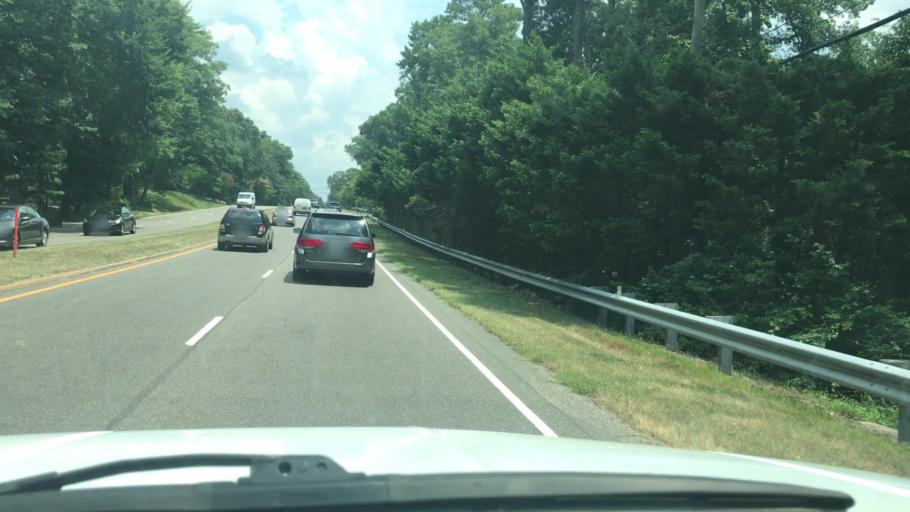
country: US
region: Virginia
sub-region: Henrico County
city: Tuckahoe
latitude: 37.5935
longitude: -77.5468
